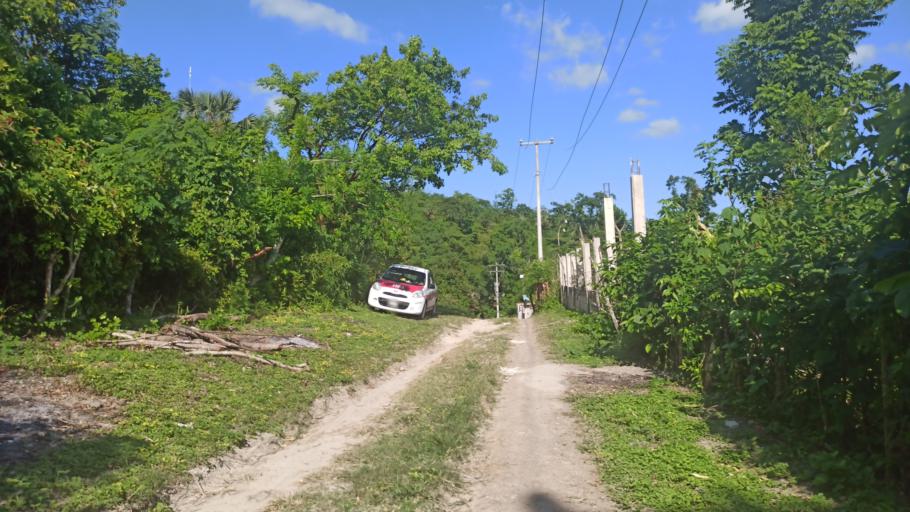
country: MX
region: Veracruz
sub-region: Papantla
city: Residencial Tajin
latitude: 20.6439
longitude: -97.3650
